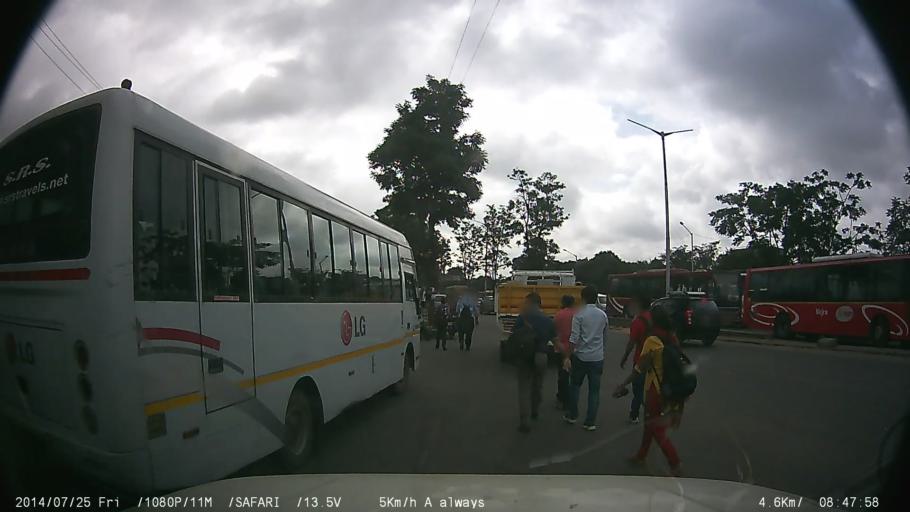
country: IN
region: Karnataka
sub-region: Bangalore Urban
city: Bangalore
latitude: 12.9177
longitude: 77.6233
